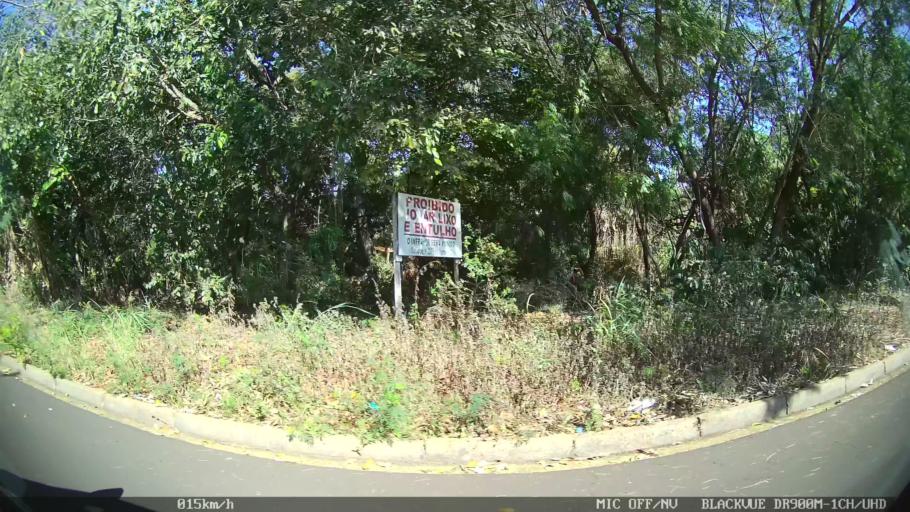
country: BR
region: Sao Paulo
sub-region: Batatais
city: Batatais
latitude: -20.8896
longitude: -47.5783
